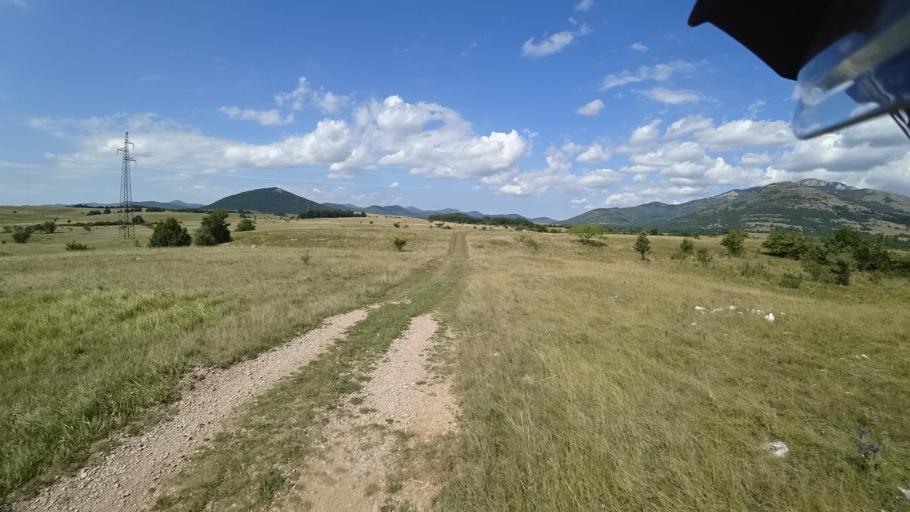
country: HR
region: Zadarska
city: Gracac
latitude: 44.4175
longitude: 15.9238
